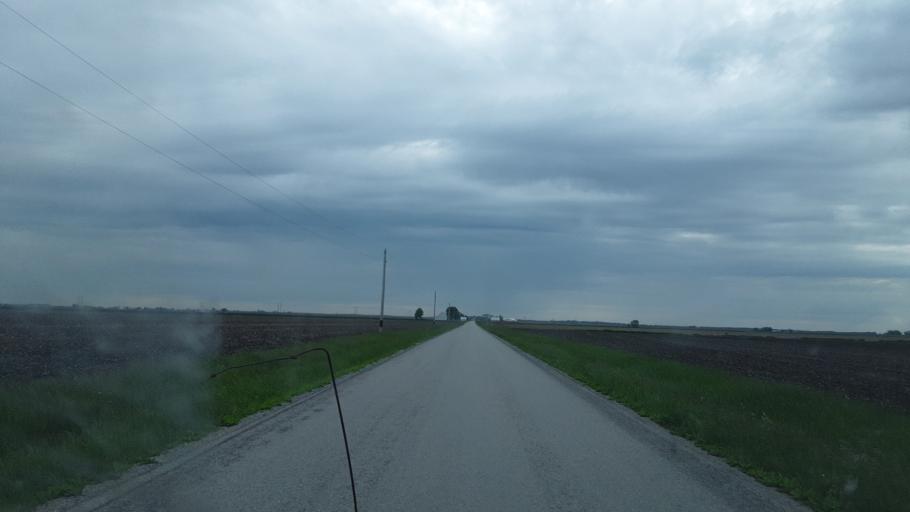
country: US
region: Illinois
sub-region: McDonough County
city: Macomb
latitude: 40.3818
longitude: -90.5430
